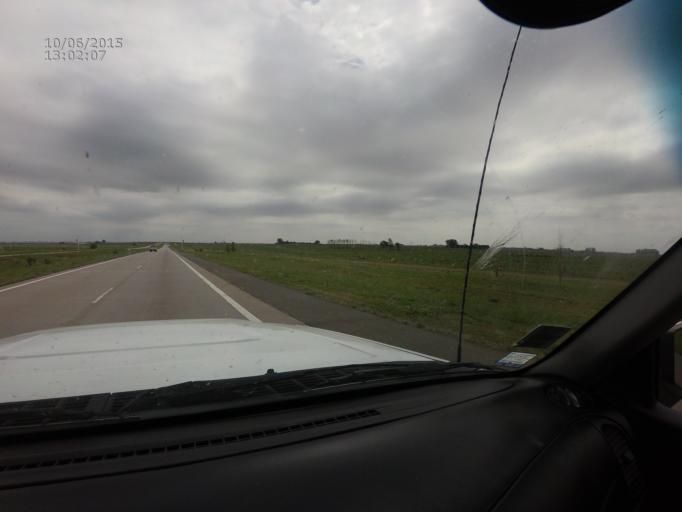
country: AR
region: Santa Fe
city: Armstrong
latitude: -32.7873
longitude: -61.7343
